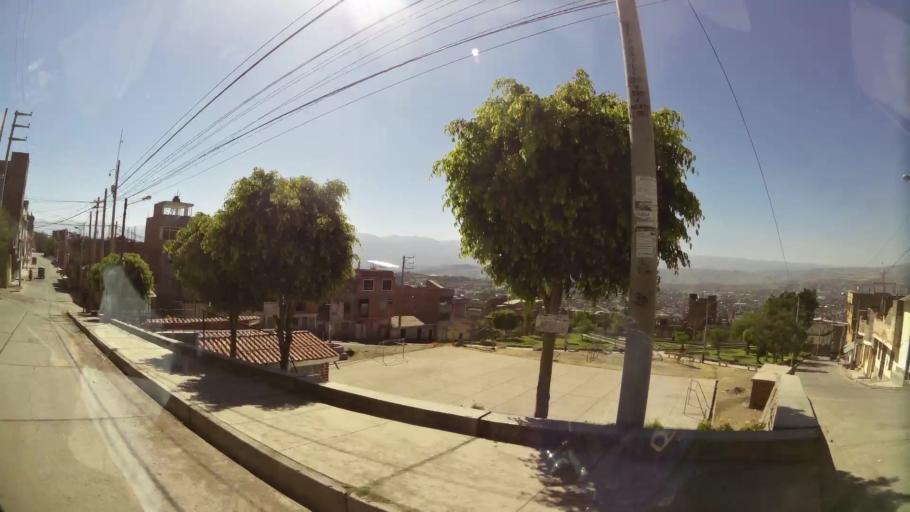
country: PE
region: Ayacucho
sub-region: Provincia de Huamanga
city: Ayacucho
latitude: -13.1567
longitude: -74.2331
